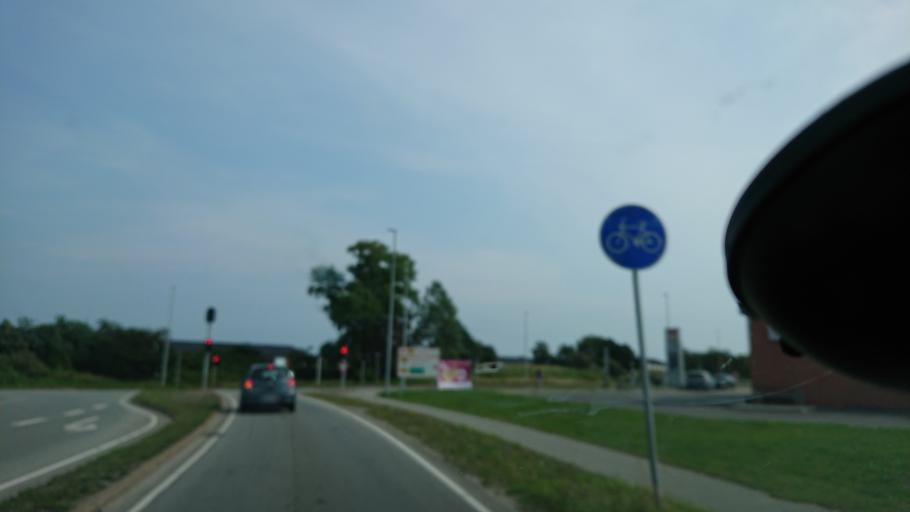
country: DK
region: North Denmark
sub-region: Frederikshavn Kommune
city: Frederikshavn
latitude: 57.4559
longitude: 10.5253
